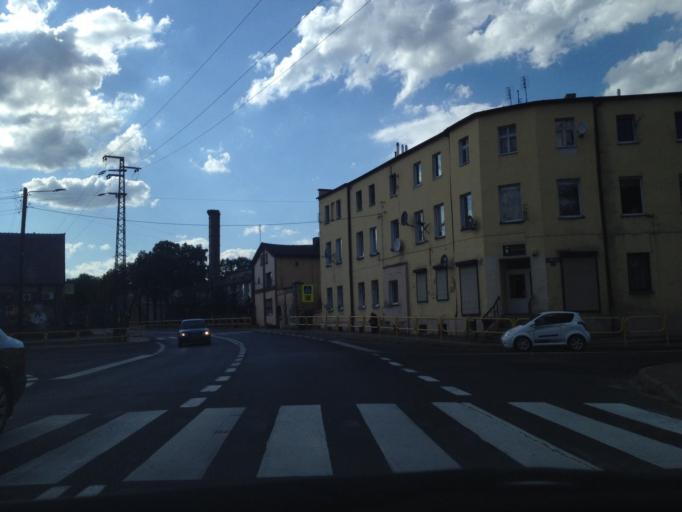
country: PL
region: Lubusz
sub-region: Powiat zarski
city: Lipinki Luzyckie
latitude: 51.6396
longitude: 15.0023
